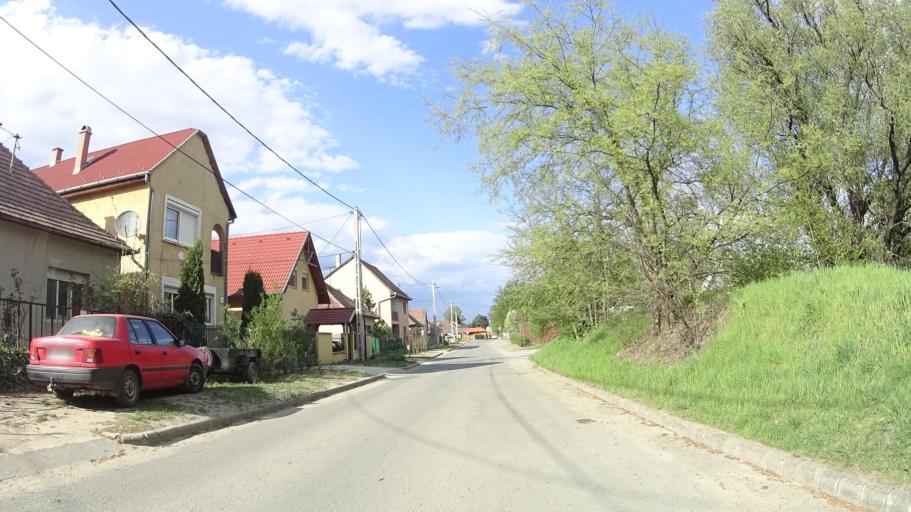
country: HU
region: Pest
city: Veresegyhaz
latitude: 47.6463
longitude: 19.2876
